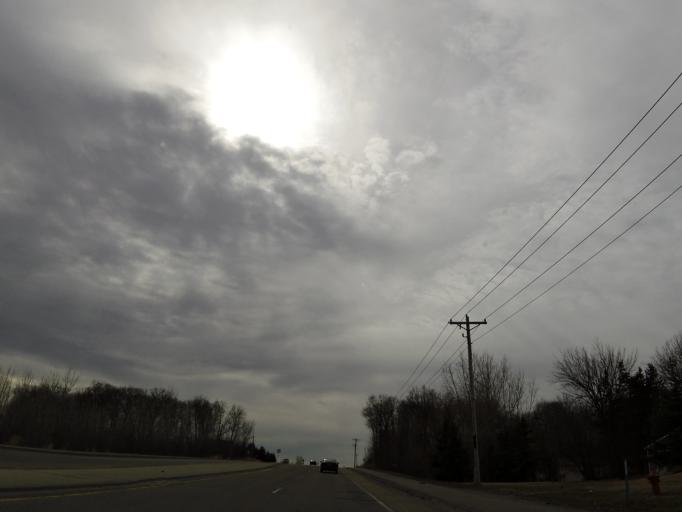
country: US
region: Minnesota
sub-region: Scott County
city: Prior Lake
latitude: 44.7307
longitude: -93.4399
